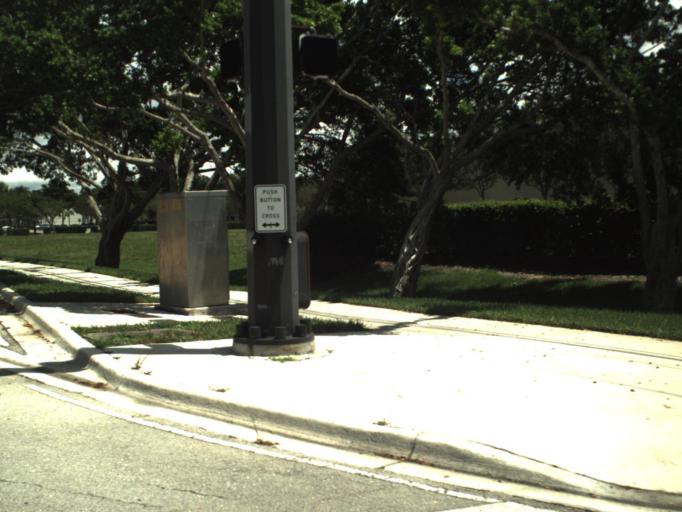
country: US
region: Florida
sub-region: Miami-Dade County
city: Country Club
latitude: 25.9803
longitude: -80.2864
